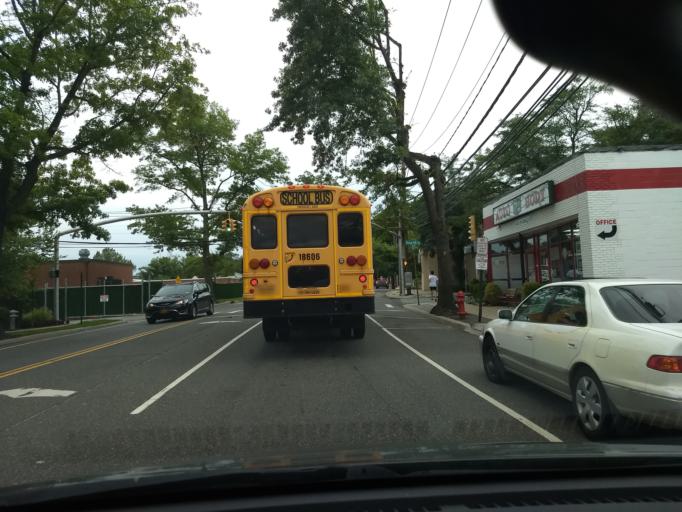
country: US
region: New York
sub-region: Nassau County
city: Kensington
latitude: 40.7965
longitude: -73.7130
